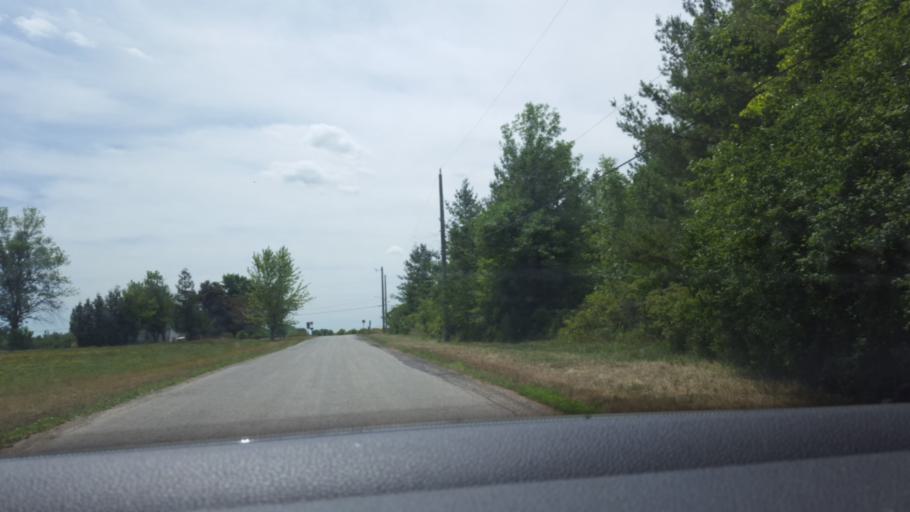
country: CA
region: Ontario
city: Hamilton
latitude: 43.1870
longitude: -79.5763
